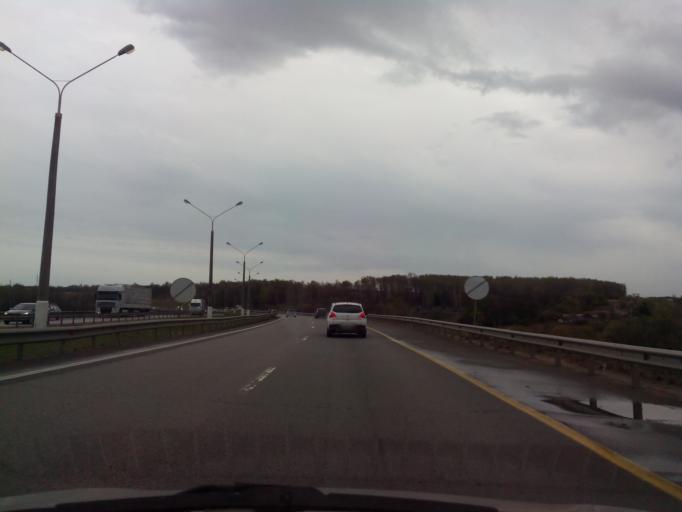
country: RU
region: Moskovskaya
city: Stupino
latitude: 54.8244
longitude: 38.0403
